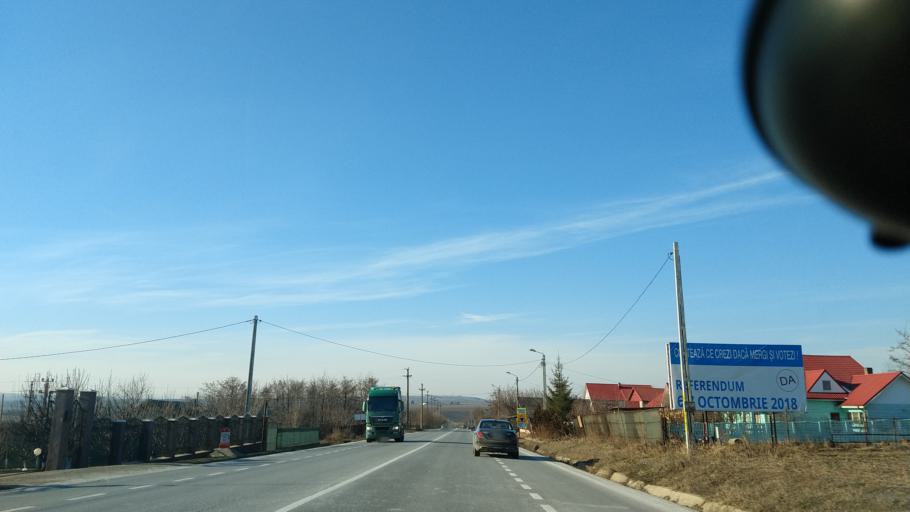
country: RO
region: Iasi
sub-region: Comuna Lungani
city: Zmeu
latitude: 47.2247
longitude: 27.1880
